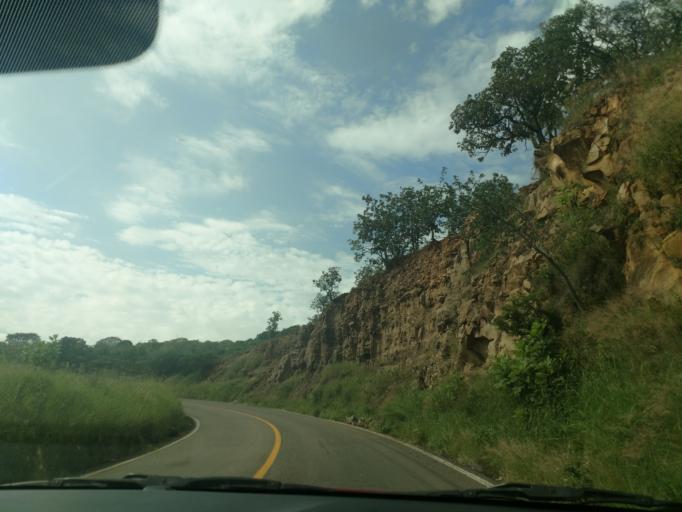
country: MX
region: Jalisco
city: El Salto
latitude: 20.3964
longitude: -104.5263
